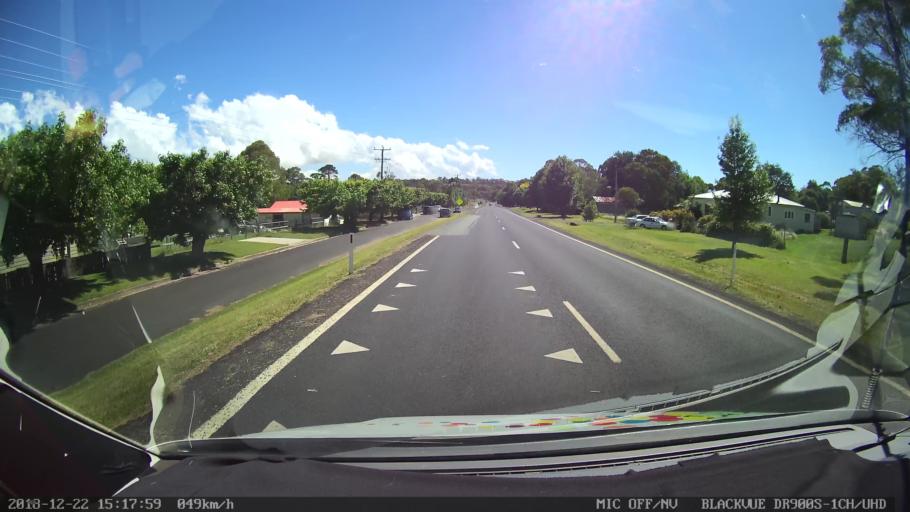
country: AU
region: New South Wales
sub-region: Bellingen
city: Dorrigo
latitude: -30.4011
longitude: 152.3504
